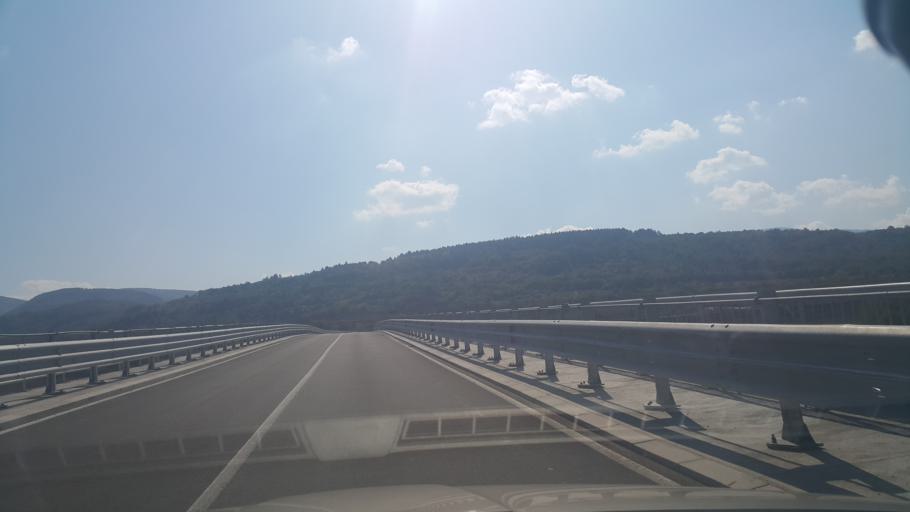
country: RS
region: Central Serbia
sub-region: Pirotski Okrug
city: Bela Palanka
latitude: 43.2293
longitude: 22.3903
